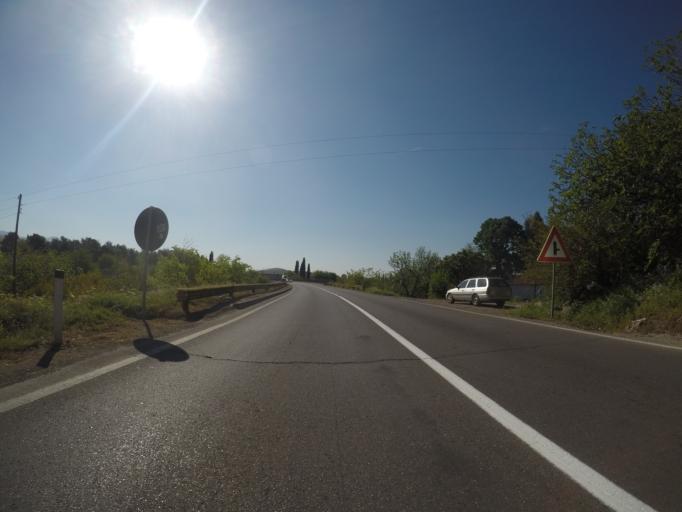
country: ME
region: Podgorica
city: Podgorica
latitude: 42.4449
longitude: 19.2032
